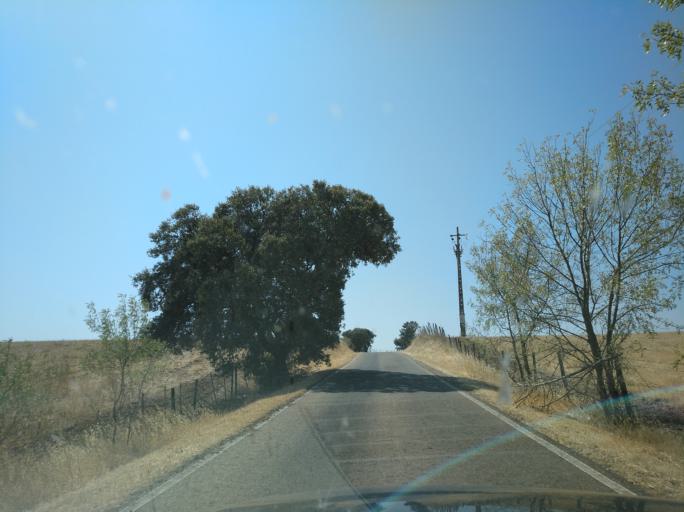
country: PT
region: Portalegre
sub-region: Campo Maior
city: Campo Maior
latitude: 39.0071
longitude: -6.9830
